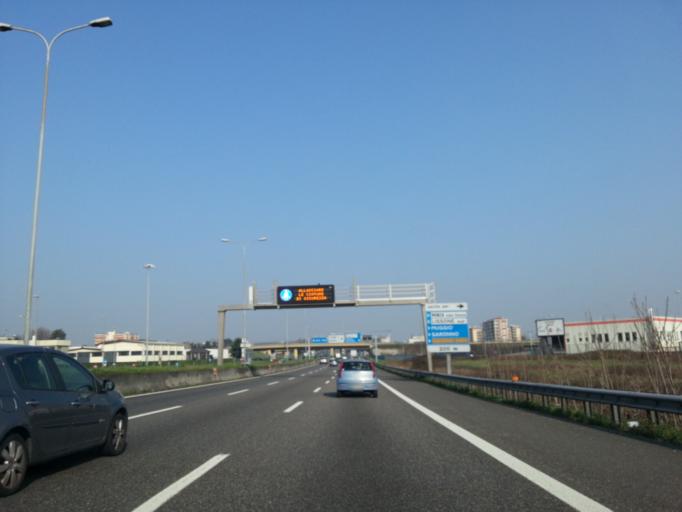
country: IT
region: Lombardy
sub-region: Provincia di Monza e Brianza
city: Muggio
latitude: 45.5933
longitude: 9.2449
